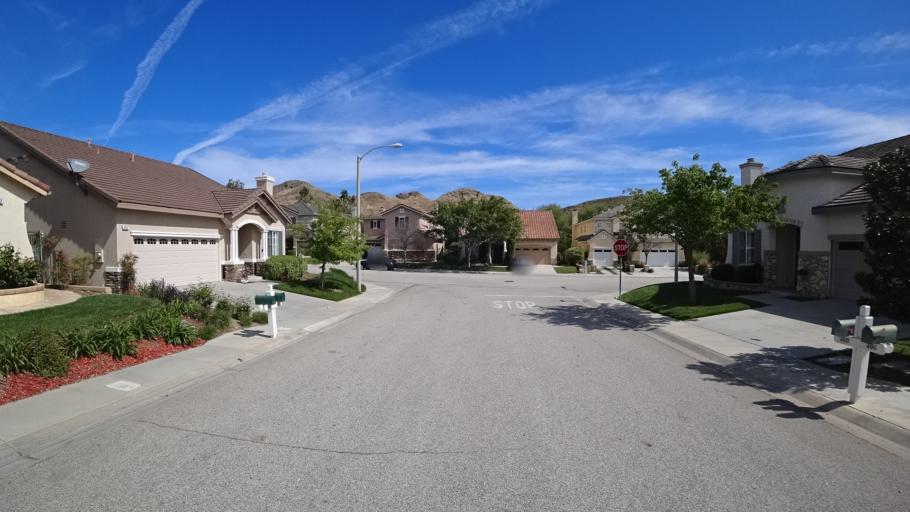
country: US
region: California
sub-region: Ventura County
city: Casa Conejo
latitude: 34.1718
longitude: -118.9737
